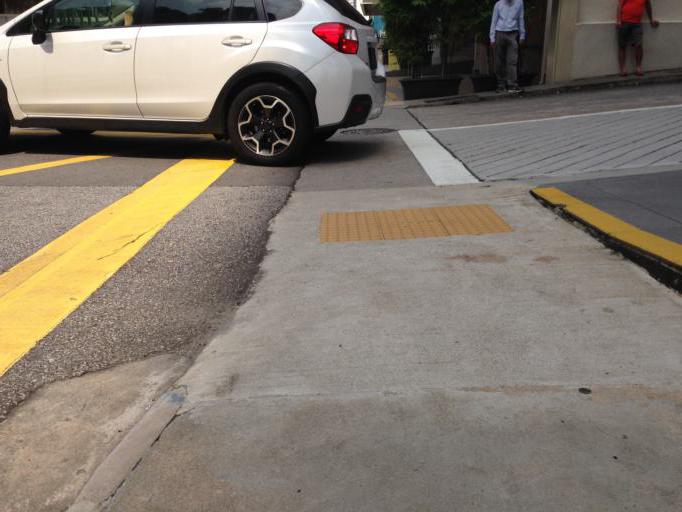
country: SG
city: Singapore
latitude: 1.3016
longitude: 103.8511
